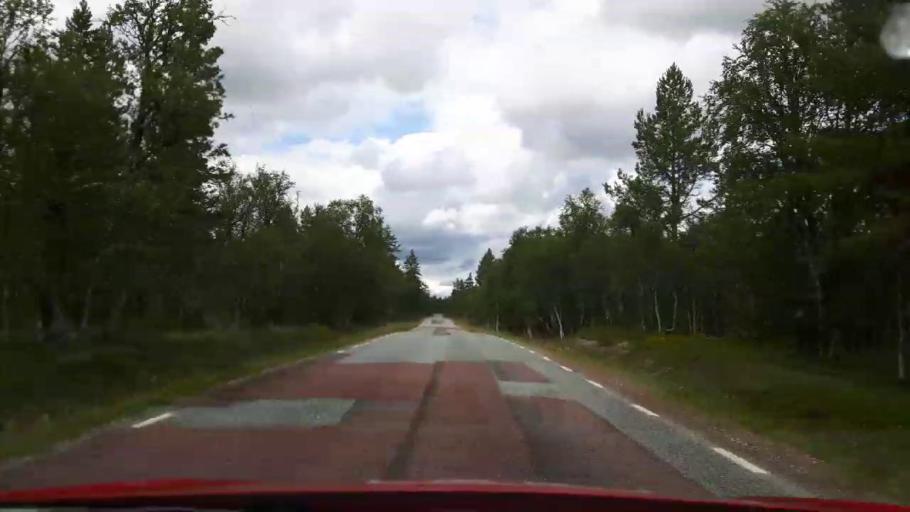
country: NO
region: Hedmark
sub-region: Trysil
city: Innbygda
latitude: 62.1217
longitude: 12.9708
